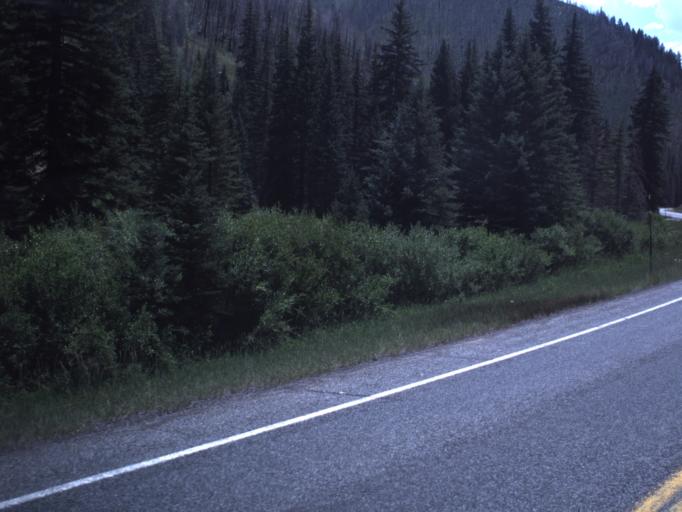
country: US
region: Utah
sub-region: Emery County
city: Huntington
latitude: 39.5227
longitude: -111.1544
